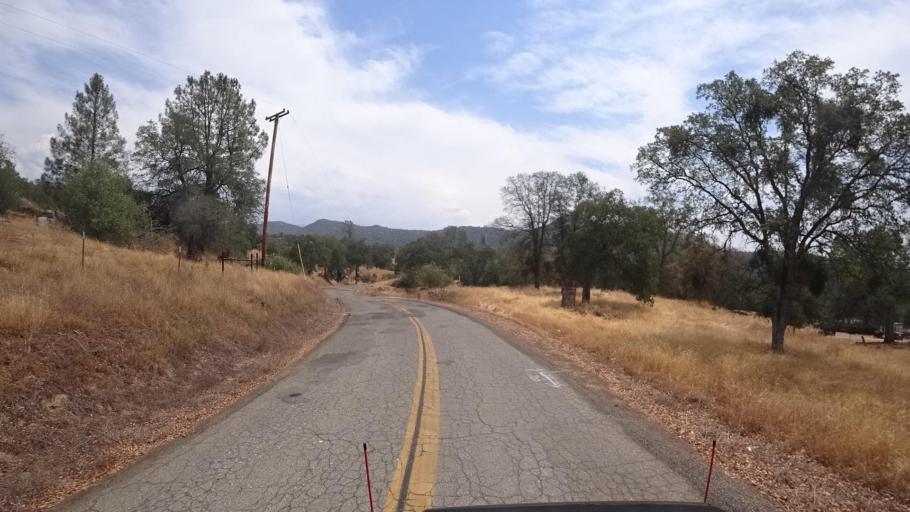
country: US
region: California
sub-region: Madera County
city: Ahwahnee
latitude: 37.3967
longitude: -119.8441
